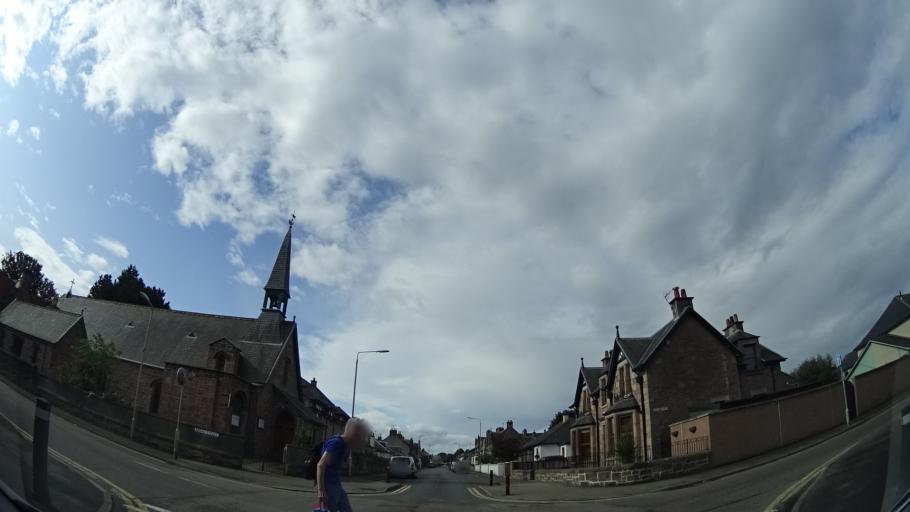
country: GB
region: Scotland
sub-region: Highland
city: Inverness
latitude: 57.4821
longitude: -4.2379
